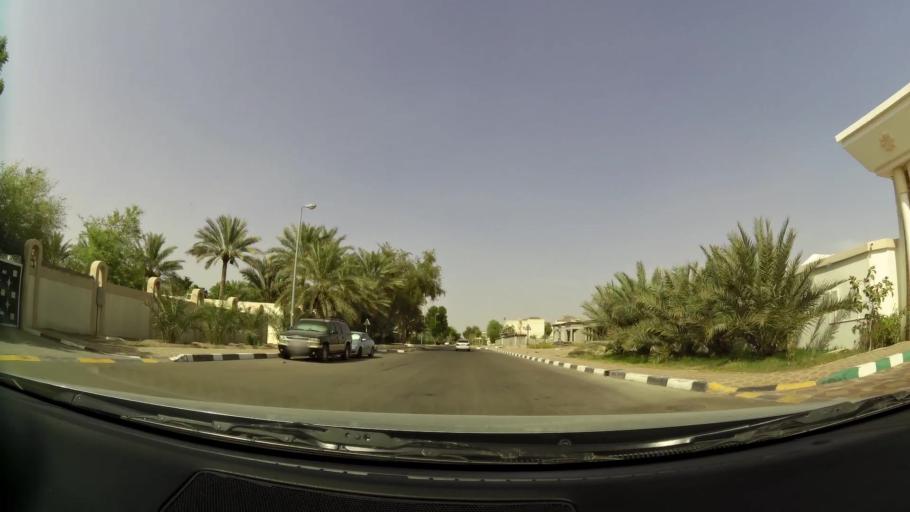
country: AE
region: Abu Dhabi
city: Al Ain
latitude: 24.2412
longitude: 55.6903
